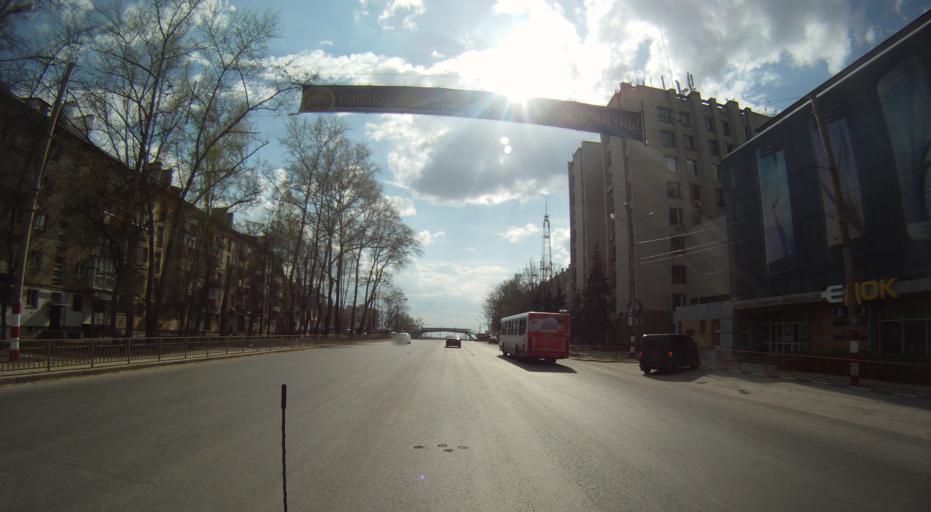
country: RU
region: Nizjnij Novgorod
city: Nizhniy Novgorod
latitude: 56.3065
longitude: 43.9834
